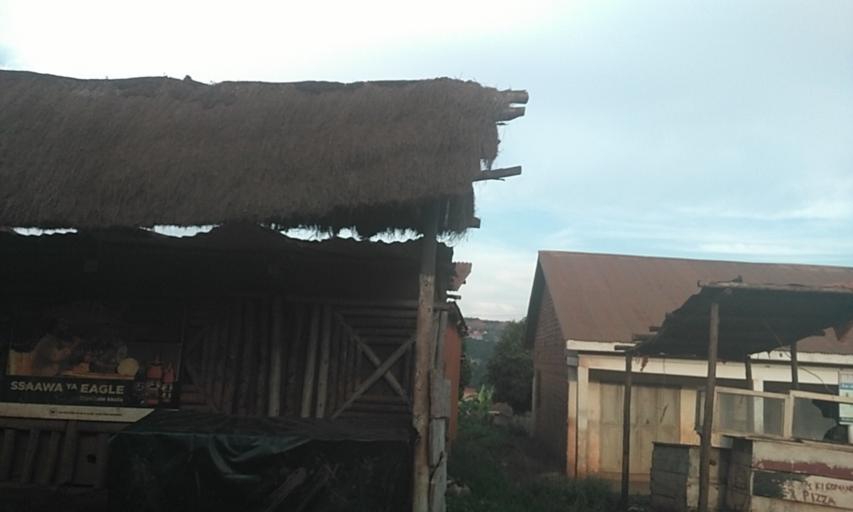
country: UG
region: Central Region
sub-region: Wakiso District
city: Kajansi
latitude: 0.2510
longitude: 32.5364
